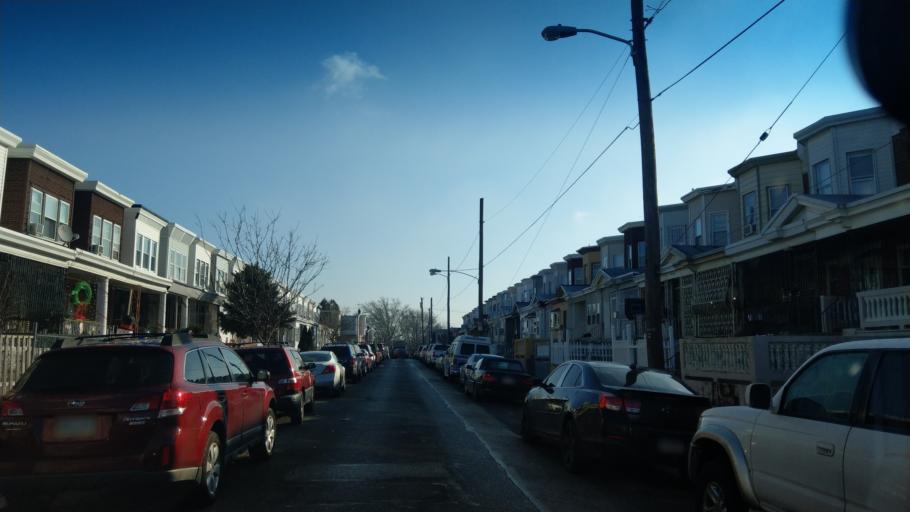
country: US
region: Pennsylvania
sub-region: Montgomery County
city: Rockledge
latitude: 40.0233
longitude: -75.1196
